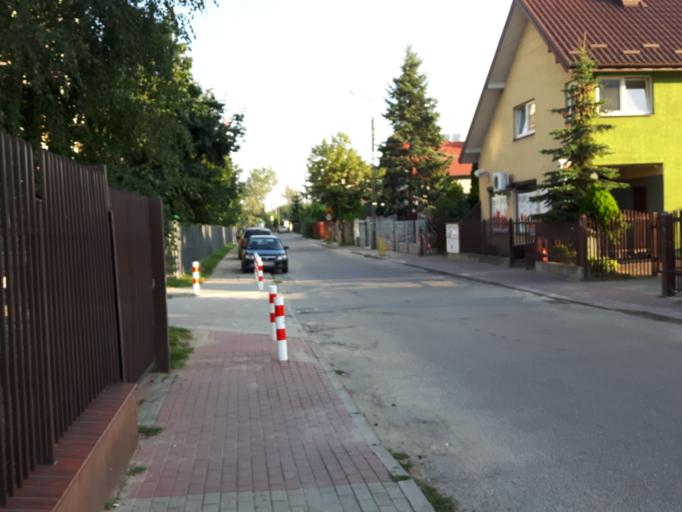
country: PL
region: Masovian Voivodeship
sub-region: Powiat wolominski
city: Zabki
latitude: 52.2862
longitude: 21.1241
